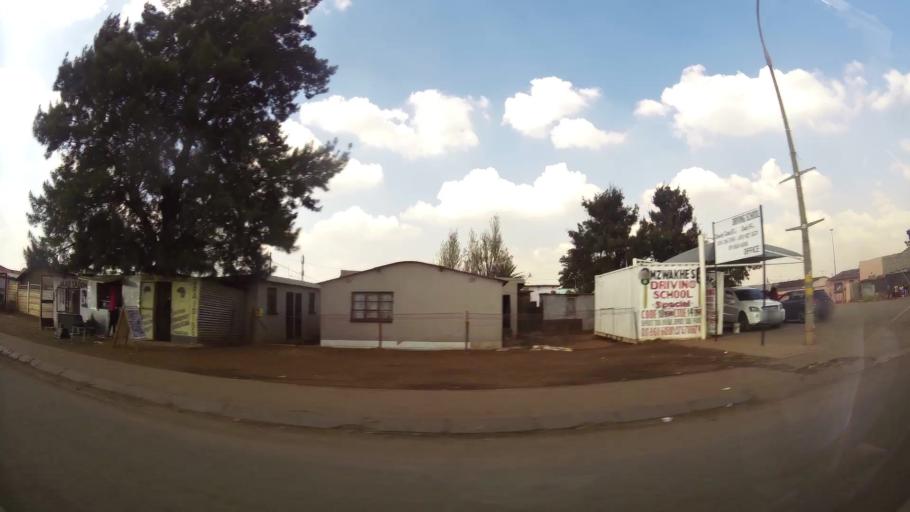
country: ZA
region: Gauteng
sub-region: Ekurhuleni Metropolitan Municipality
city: Germiston
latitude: -26.3364
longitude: 28.1412
